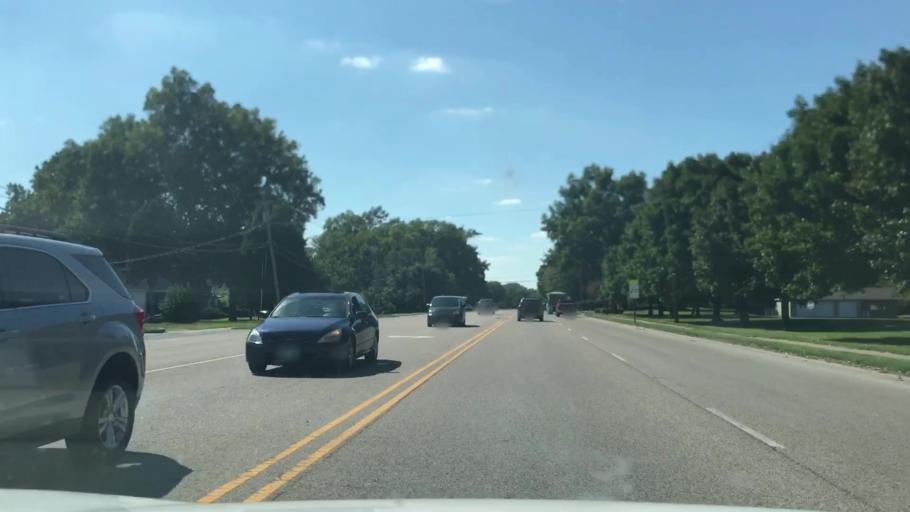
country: US
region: Illinois
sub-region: Saint Clair County
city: Swansea
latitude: 38.5418
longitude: -90.0373
